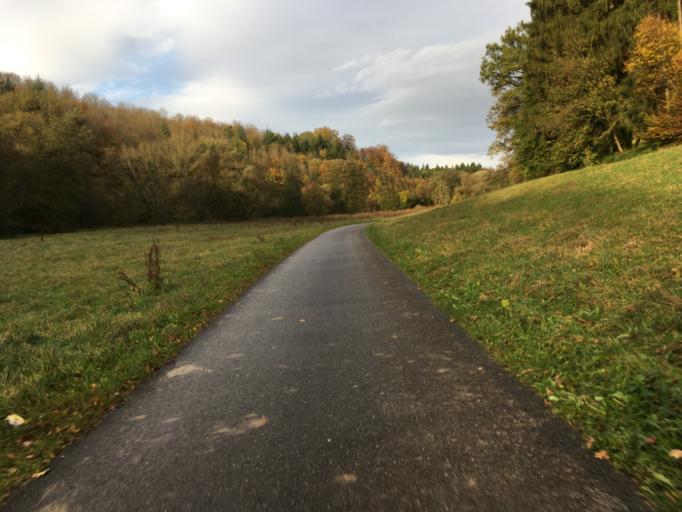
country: DE
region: Baden-Wuerttemberg
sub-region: Regierungsbezirk Stuttgart
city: Jagsthausen
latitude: 49.3554
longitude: 9.4651
